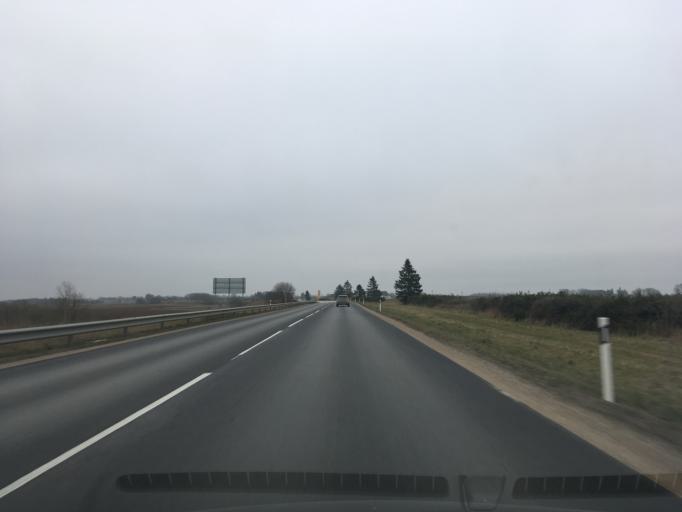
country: EE
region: Ida-Virumaa
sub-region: Aseri vald
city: Aseri
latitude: 59.4422
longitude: 26.7980
